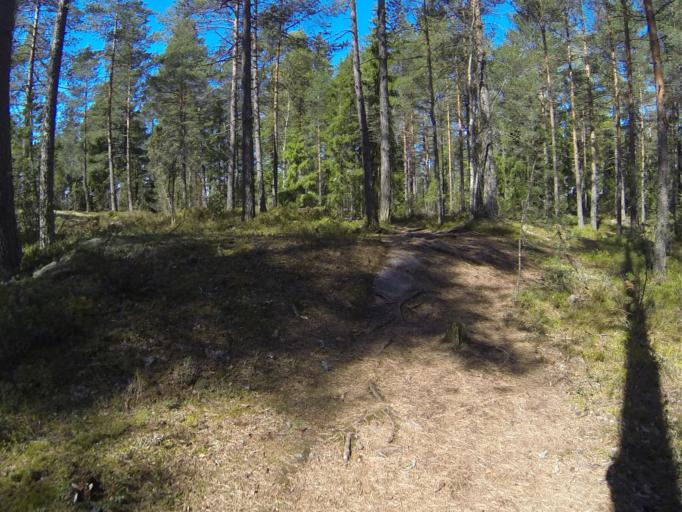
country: FI
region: Varsinais-Suomi
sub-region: Salo
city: Salo
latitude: 60.3999
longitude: 23.1930
